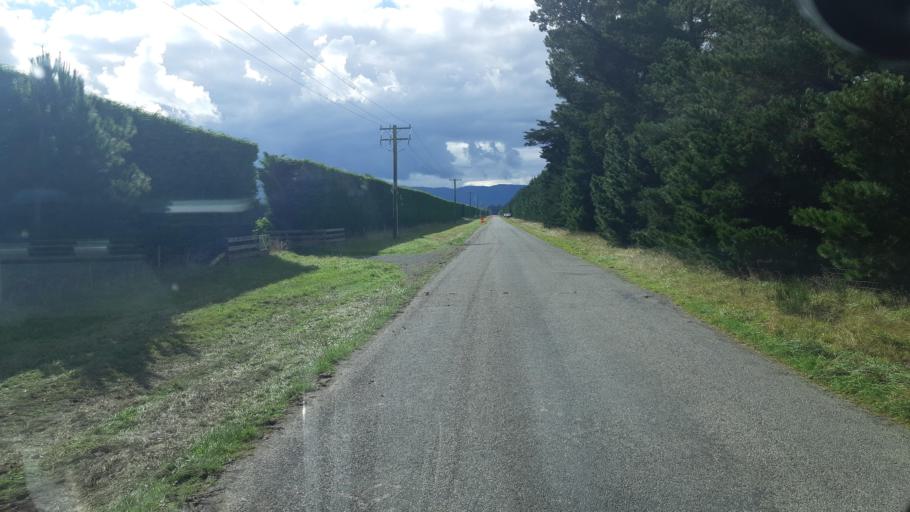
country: NZ
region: Canterbury
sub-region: Waimakariri District
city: Oxford
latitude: -43.3293
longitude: 172.1744
